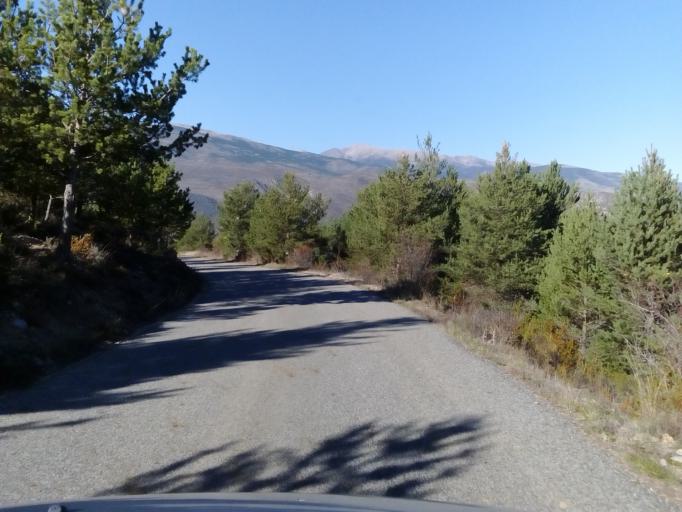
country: ES
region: Catalonia
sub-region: Provincia de Lleida
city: Bellver de Cerdanya
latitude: 42.3471
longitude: 1.7771
